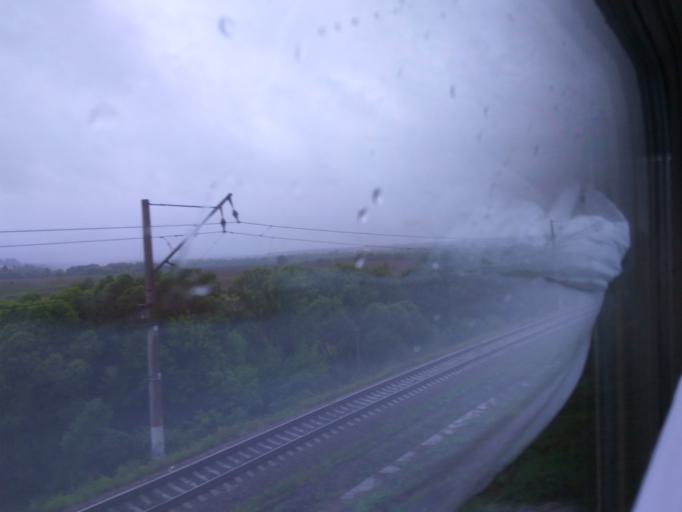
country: RU
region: Moskovskaya
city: Kashira
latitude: 54.8563
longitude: 38.1751
